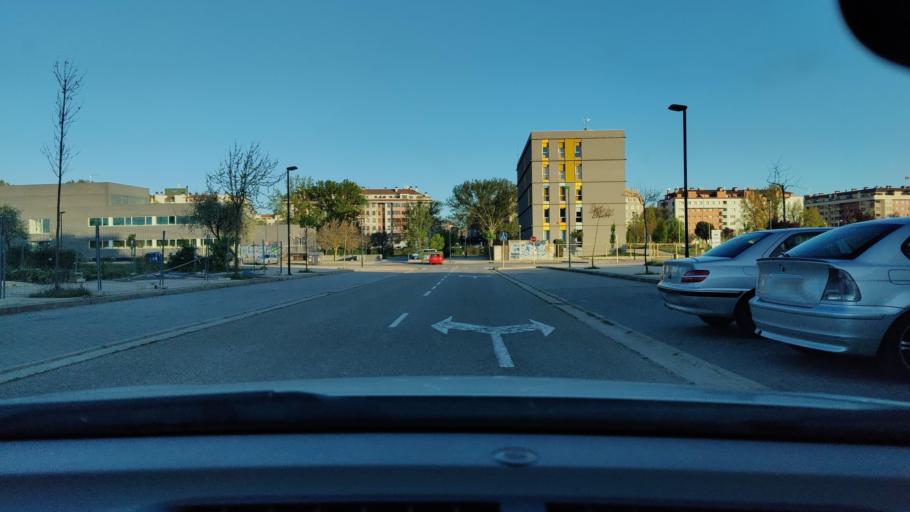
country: ES
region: Castille and Leon
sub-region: Provincia de Burgos
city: Burgos
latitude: 42.3642
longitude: -3.6681
